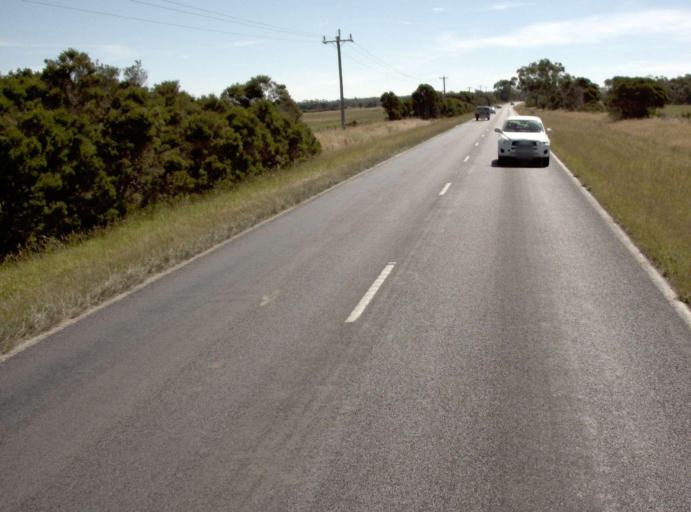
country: AU
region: Victoria
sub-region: Latrobe
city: Morwell
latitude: -38.6345
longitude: 146.5389
